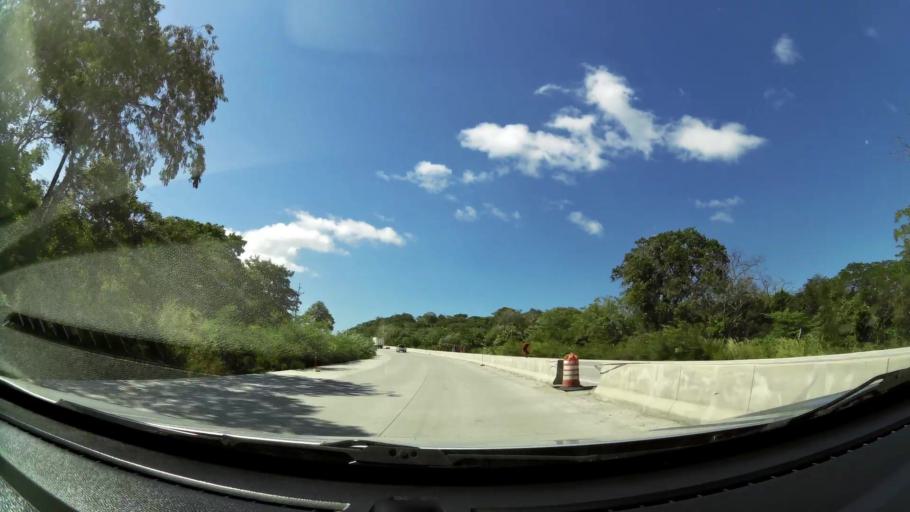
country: CR
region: Guanacaste
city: Bagaces
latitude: 10.5363
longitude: -85.2902
